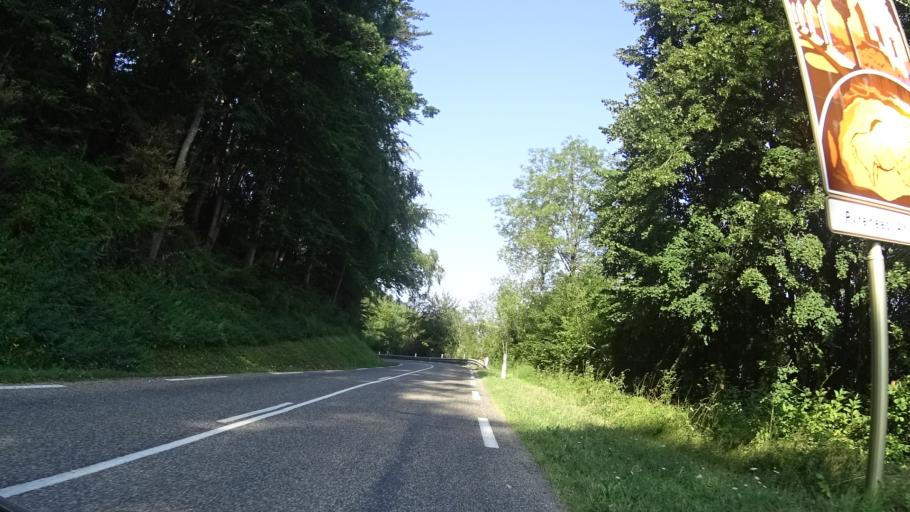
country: FR
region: Midi-Pyrenees
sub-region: Departement de l'Ariege
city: Belesta
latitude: 42.9111
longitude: 1.9827
